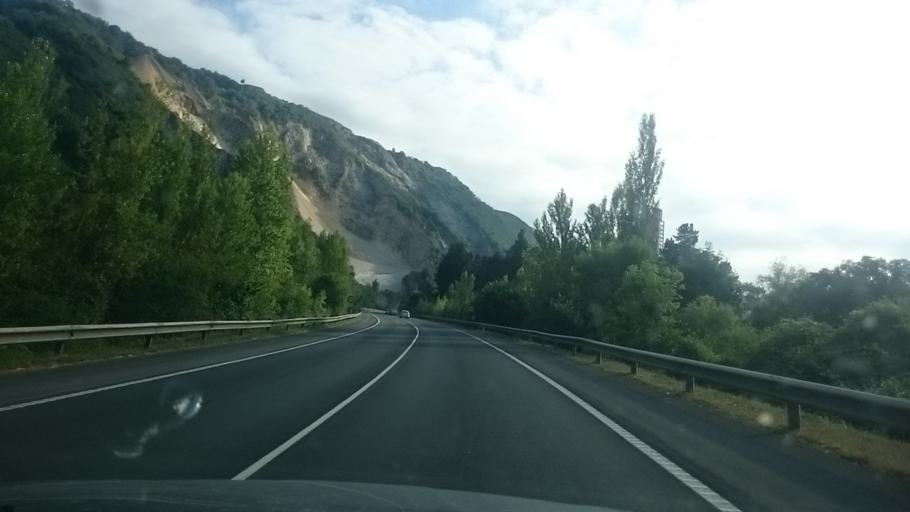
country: ES
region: Asturias
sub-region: Province of Asturias
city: Oviedo
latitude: 43.3323
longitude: -5.7701
